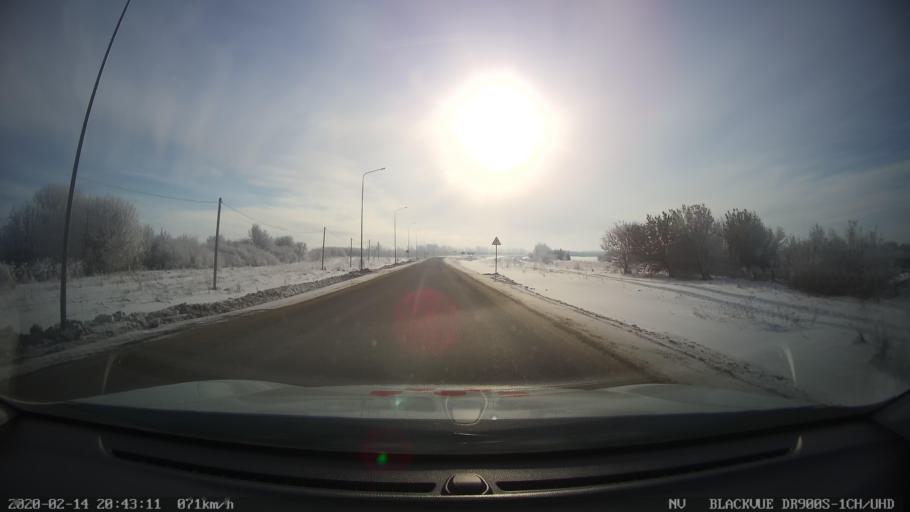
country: RU
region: Tatarstan
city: Kuybyshevskiy Zaton
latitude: 55.3107
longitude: 49.1457
